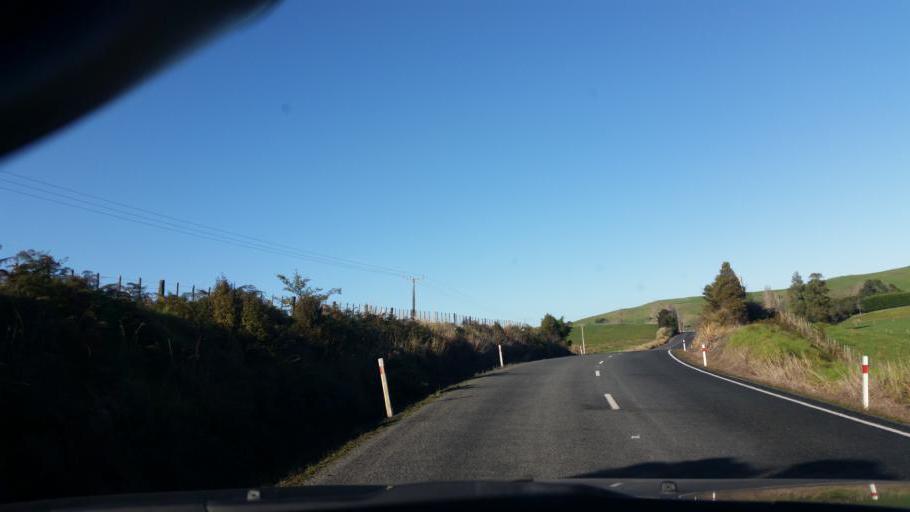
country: NZ
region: Northland
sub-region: Kaipara District
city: Dargaville
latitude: -35.8158
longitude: 173.9255
